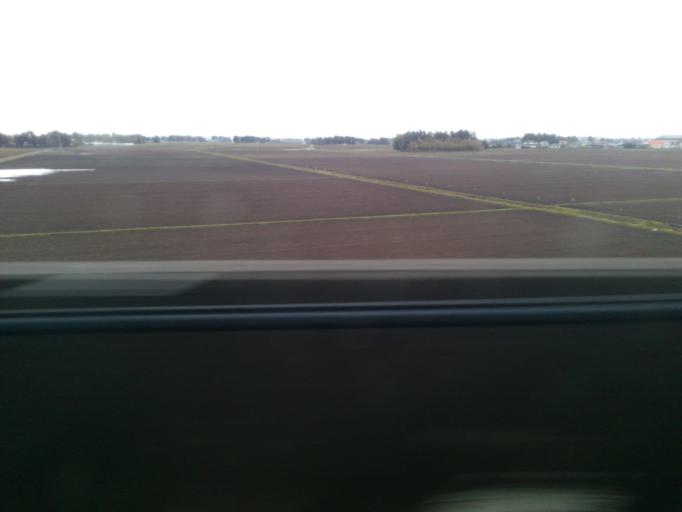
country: JP
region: Miyagi
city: Furukawa
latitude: 38.6001
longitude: 140.9824
